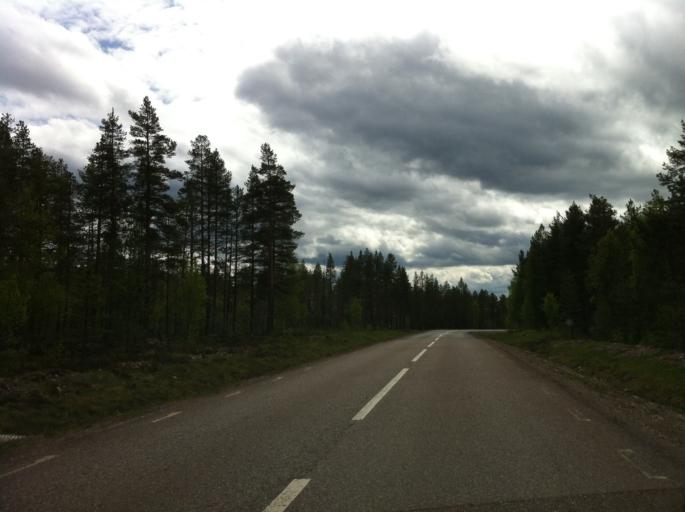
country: NO
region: Hedmark
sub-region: Trysil
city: Innbygda
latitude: 61.5313
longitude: 13.0815
